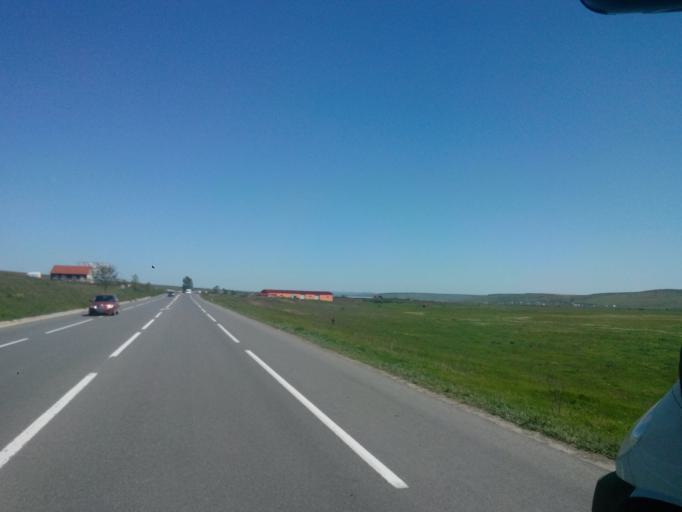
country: RO
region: Iasi
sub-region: Comuna Dumesti
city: Dumesti
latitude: 47.2137
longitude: 27.3395
